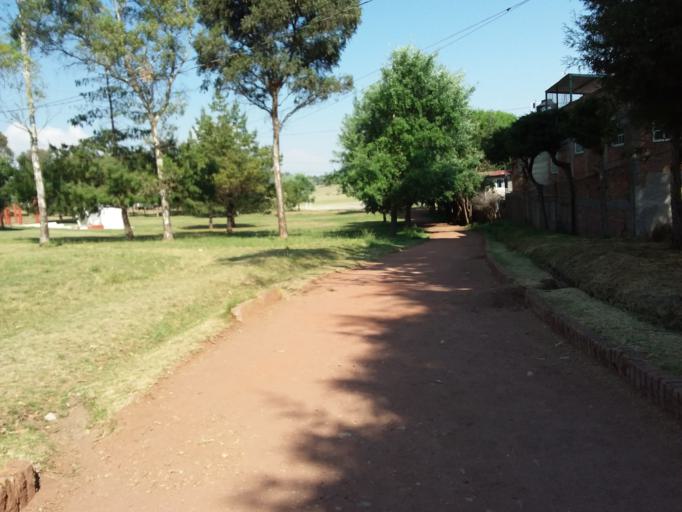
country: MX
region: Mexico
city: San Buenaventura
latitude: 19.2756
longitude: -99.6899
